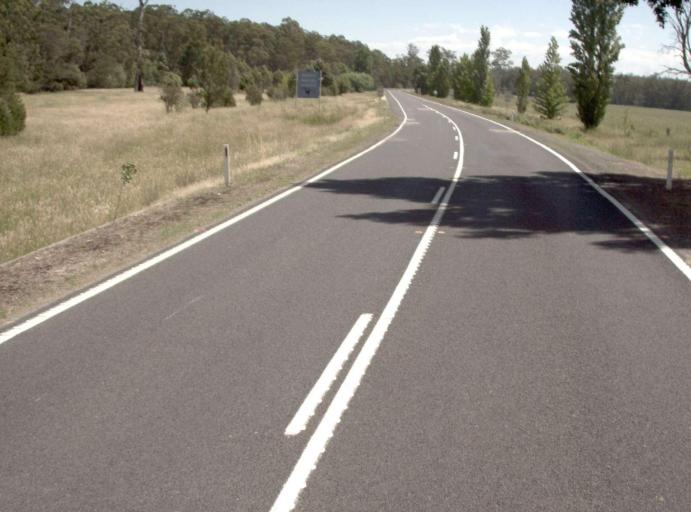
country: AU
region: New South Wales
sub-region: Bombala
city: Bombala
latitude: -37.5667
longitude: 149.1438
